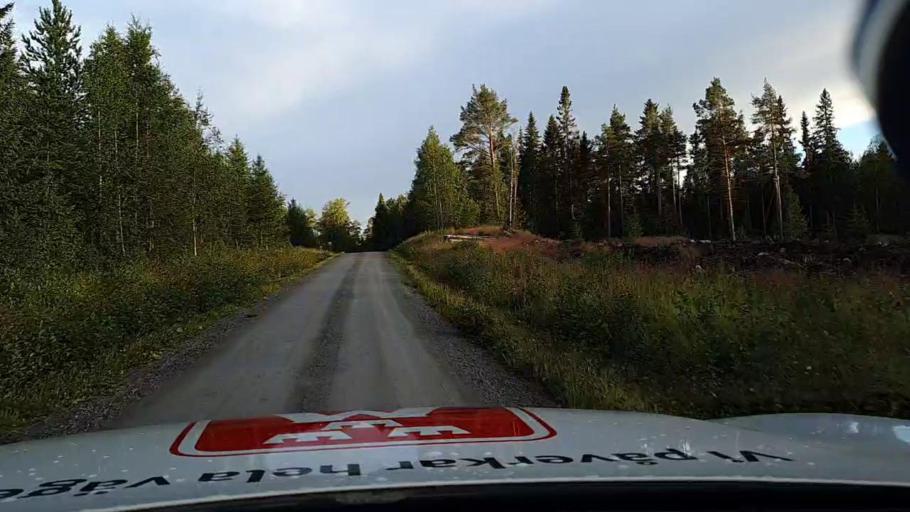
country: SE
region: Jaemtland
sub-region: Bergs Kommun
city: Hoverberg
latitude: 62.8559
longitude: 14.5360
